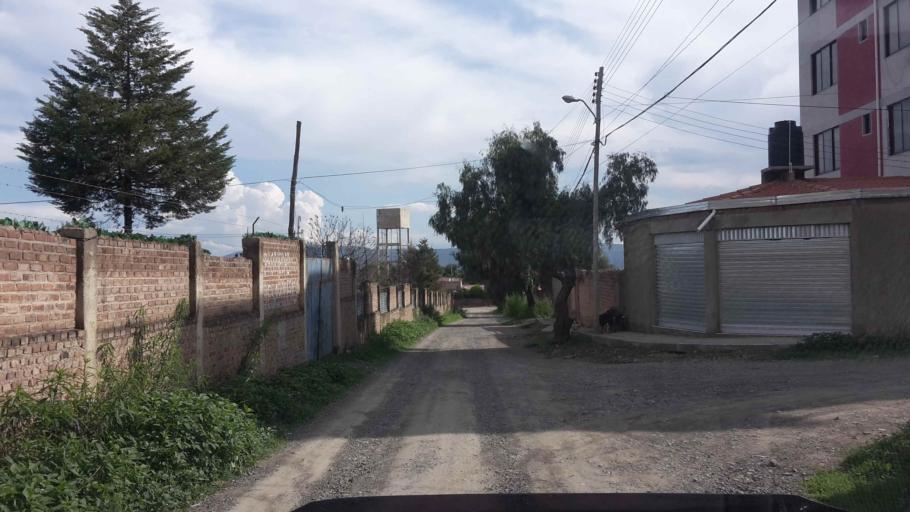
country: BO
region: Cochabamba
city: Cochabamba
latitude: -17.3340
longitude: -66.2146
